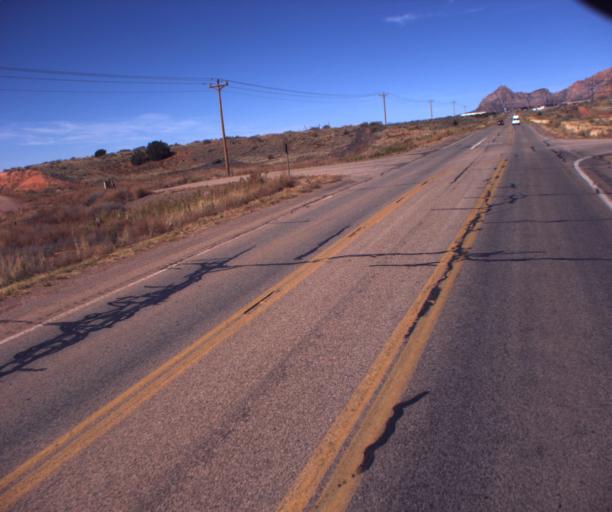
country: US
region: Arizona
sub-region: Mohave County
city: Colorado City
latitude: 36.9901
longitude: -112.9907
